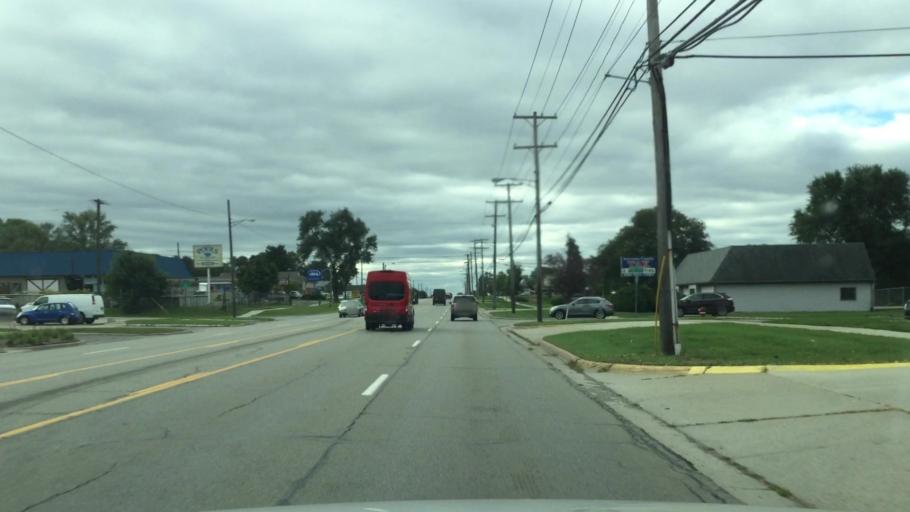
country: US
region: Michigan
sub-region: Macomb County
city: Shelby
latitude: 42.6514
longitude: -83.0334
